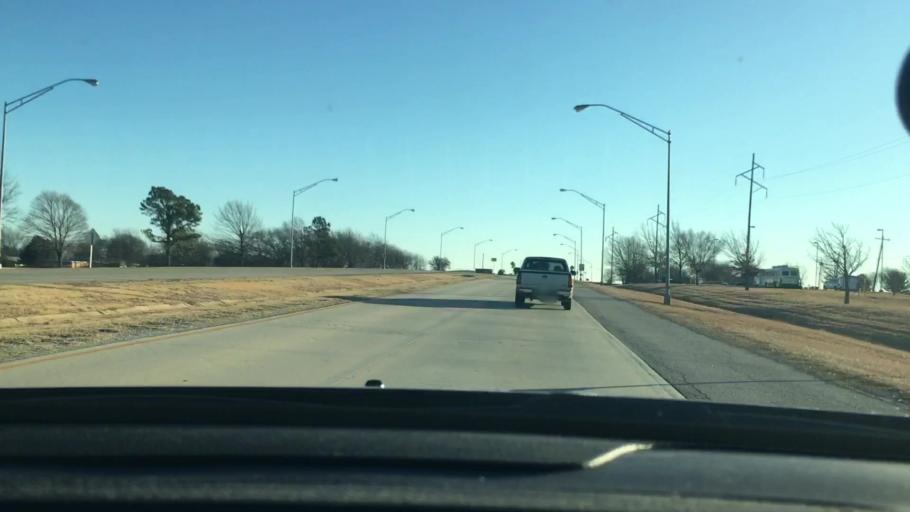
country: US
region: Oklahoma
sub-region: Carter County
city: Ardmore
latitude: 34.2023
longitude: -97.1499
